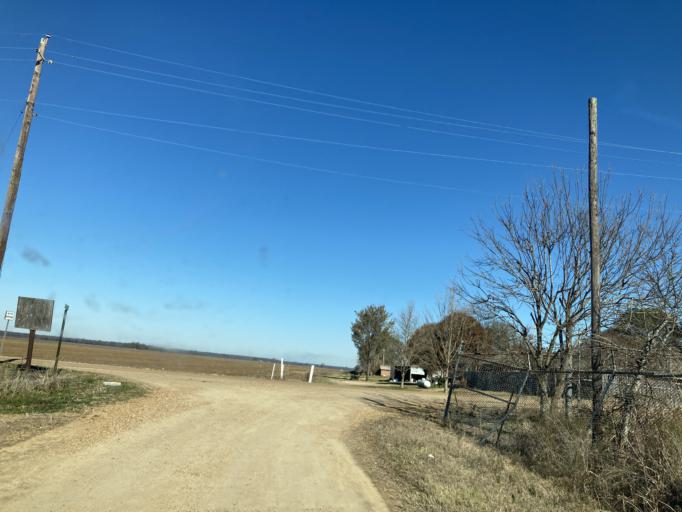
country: US
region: Mississippi
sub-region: Sharkey County
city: Rolling Fork
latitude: 32.8213
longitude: -90.7117
